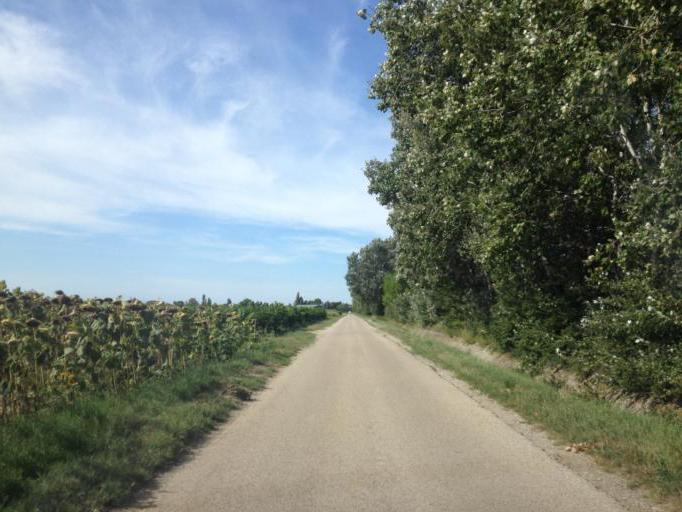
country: FR
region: Provence-Alpes-Cote d'Azur
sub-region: Departement du Vaucluse
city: Courthezon
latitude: 44.0728
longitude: 4.8824
